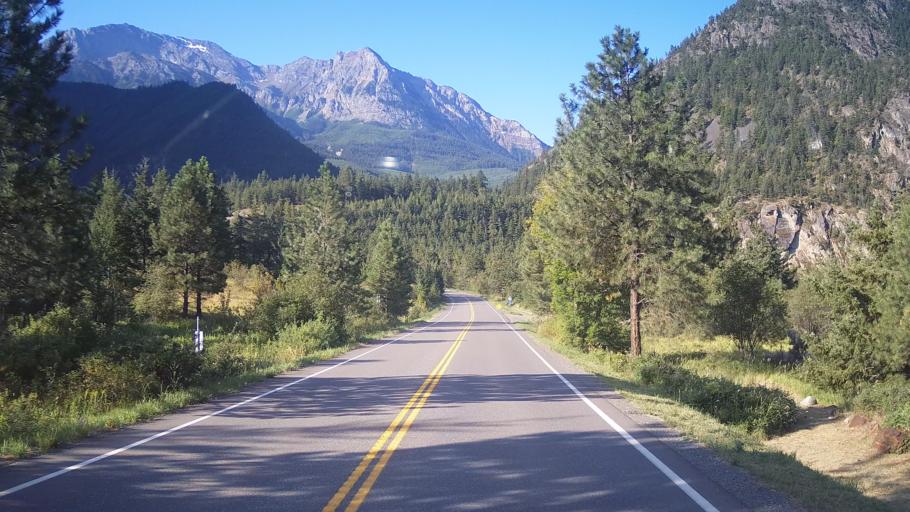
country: CA
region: British Columbia
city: Lillooet
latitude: 50.6672
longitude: -121.9872
